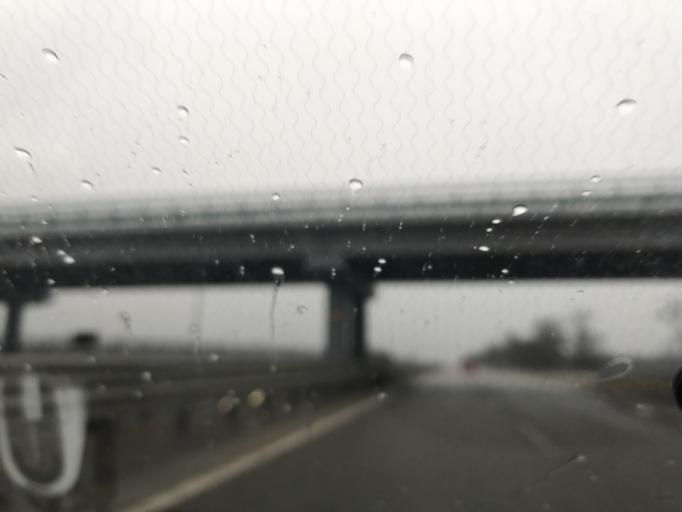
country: RU
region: Krasnodarskiy
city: Kislyakovskaya
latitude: 46.3582
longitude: 39.7654
